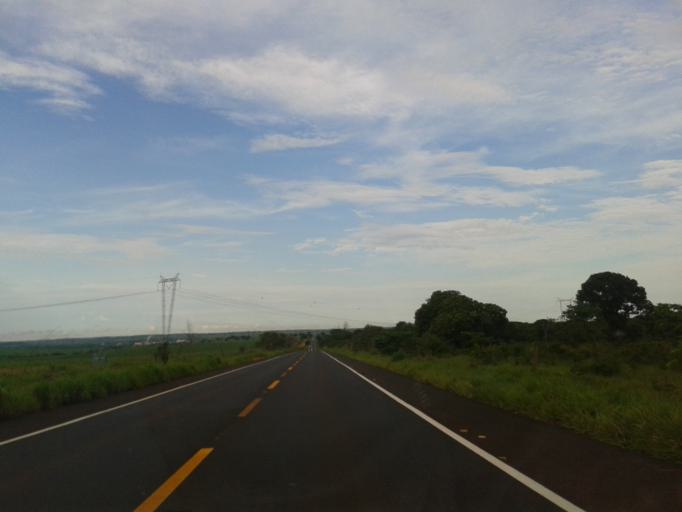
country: BR
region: Minas Gerais
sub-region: Santa Vitoria
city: Santa Vitoria
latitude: -19.0449
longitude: -50.4559
